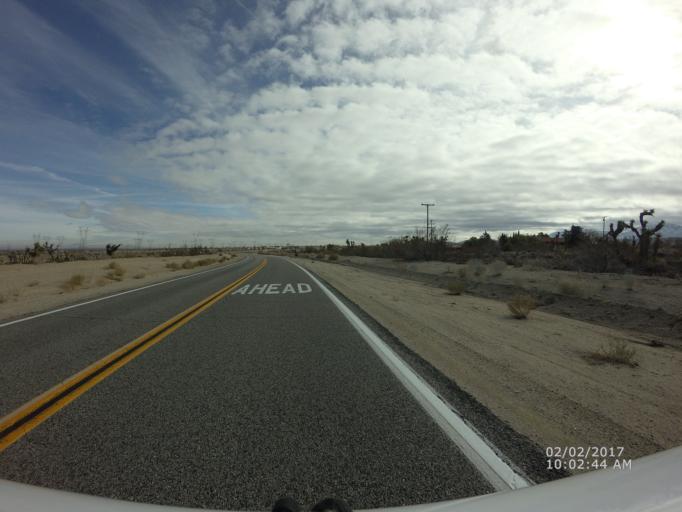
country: US
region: California
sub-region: Los Angeles County
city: Littlerock
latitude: 34.5067
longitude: -117.9719
